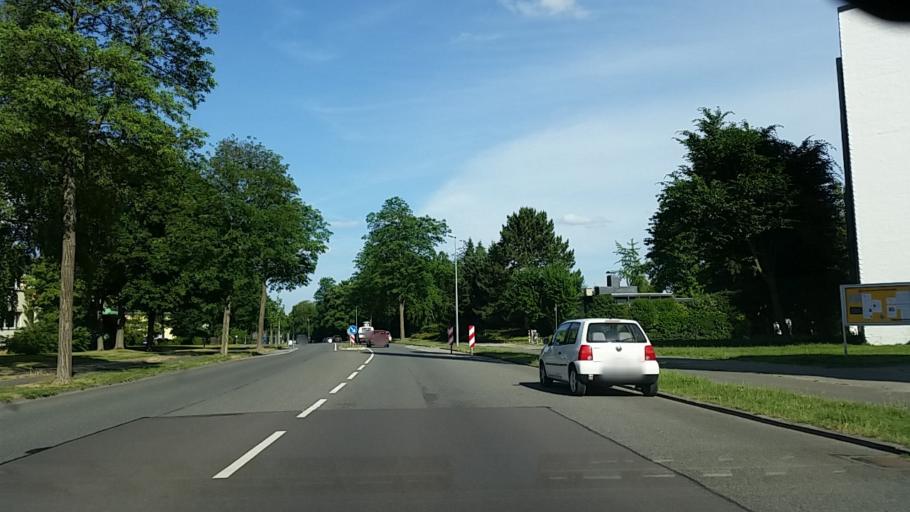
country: DE
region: Lower Saxony
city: Wolfsburg
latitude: 52.4099
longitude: 10.7694
